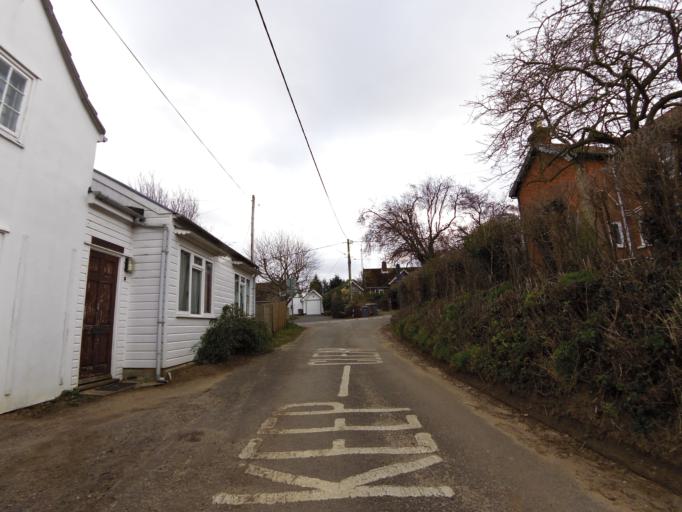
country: GB
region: England
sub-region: Suffolk
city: Woodbridge
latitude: 52.0531
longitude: 1.3274
